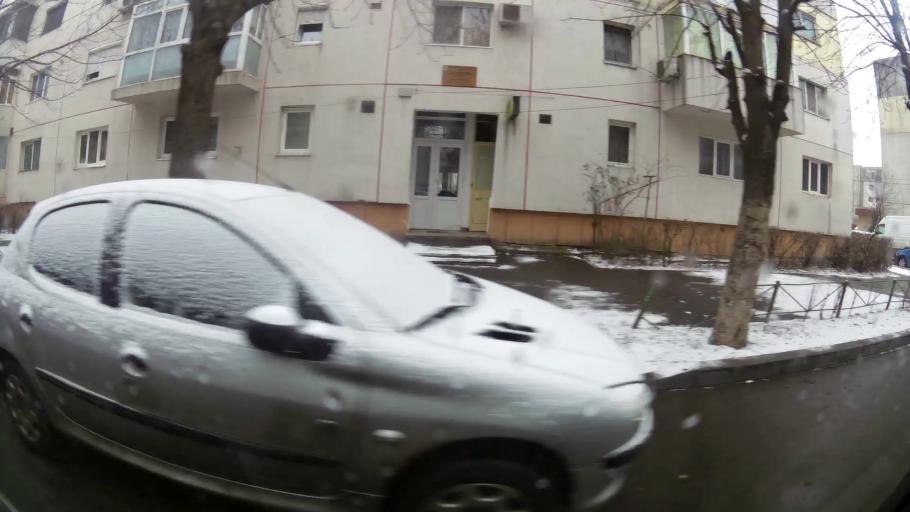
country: RO
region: Prahova
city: Ploiesti
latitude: 44.9416
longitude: 25.9977
